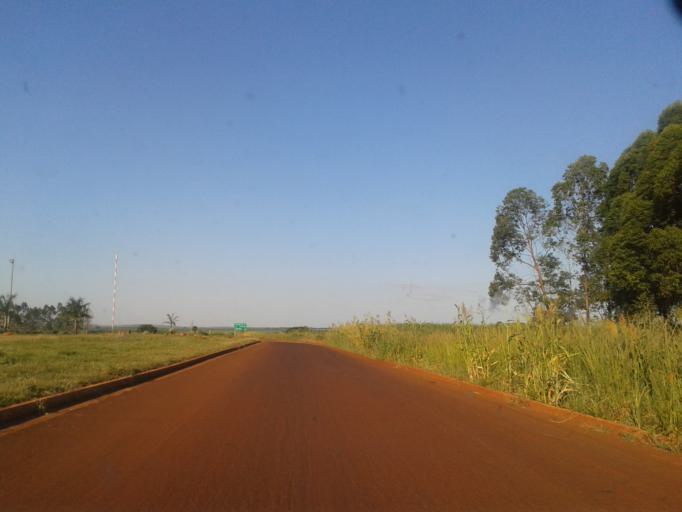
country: BR
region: Minas Gerais
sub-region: Capinopolis
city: Capinopolis
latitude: -18.7055
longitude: -49.6865
